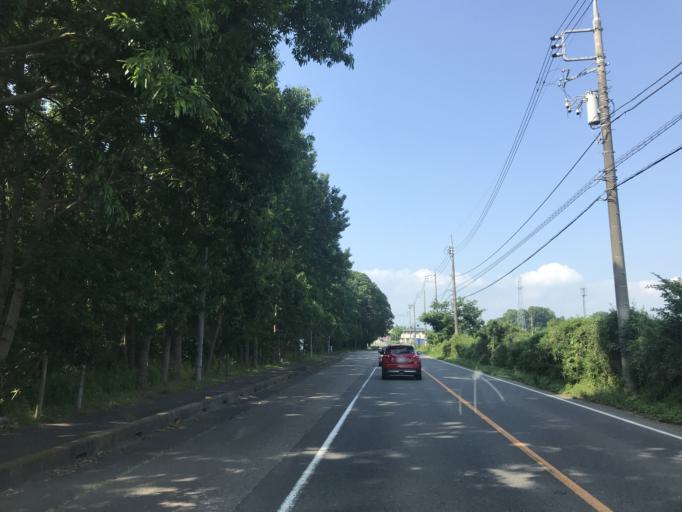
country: JP
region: Ibaraki
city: Naka
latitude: 36.0639
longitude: 140.0937
